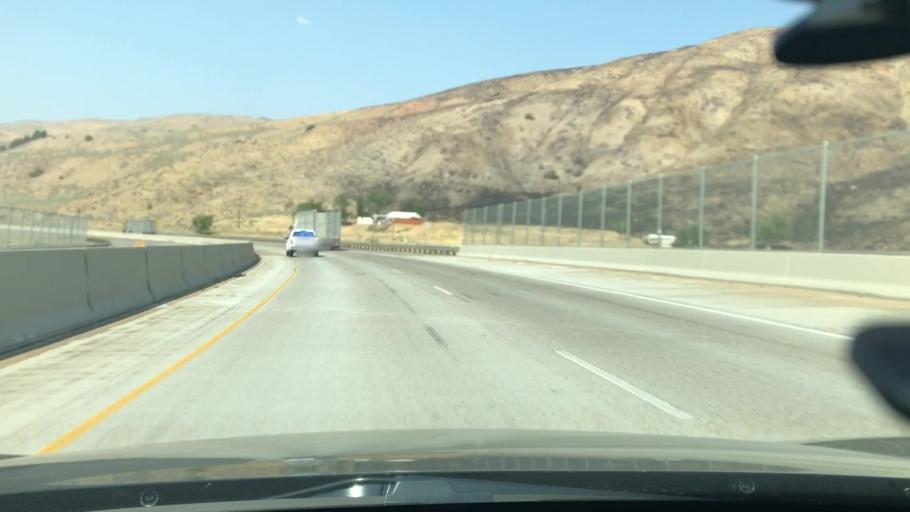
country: US
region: Idaho
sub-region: Washington County
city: Weiser
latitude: 44.4119
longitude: -117.3082
